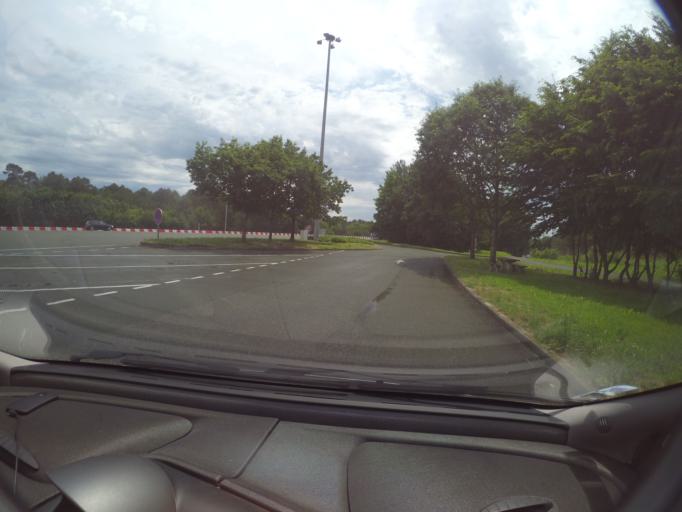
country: FR
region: Pays de la Loire
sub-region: Departement de Maine-et-Loire
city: Seiches-sur-le-Loir
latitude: 47.5380
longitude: -0.3425
